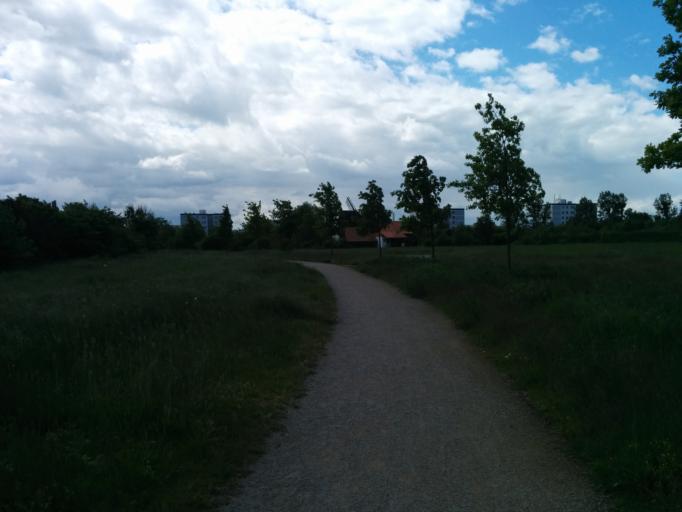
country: DE
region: Lower Saxony
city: Wolfsburg
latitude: 52.4501
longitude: 10.7859
